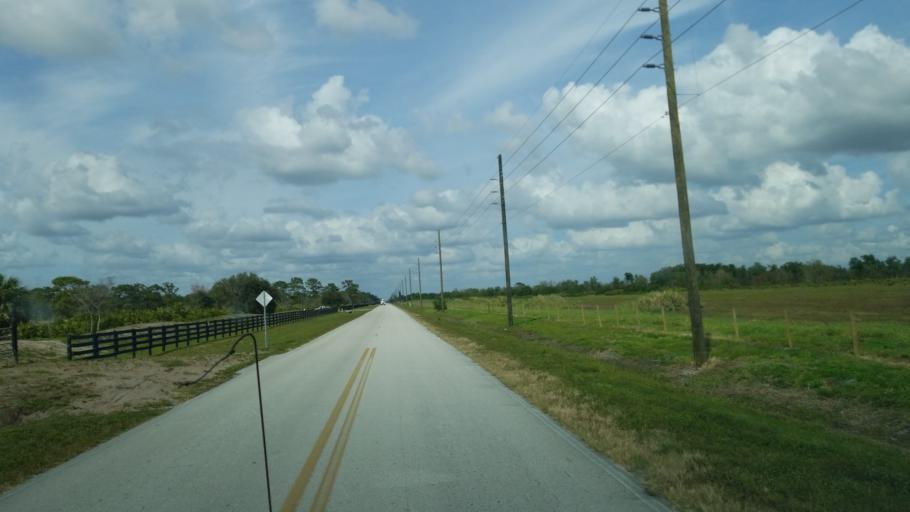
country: US
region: Florida
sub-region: Okeechobee County
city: Cypress Quarters
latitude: 27.4706
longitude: -80.7709
